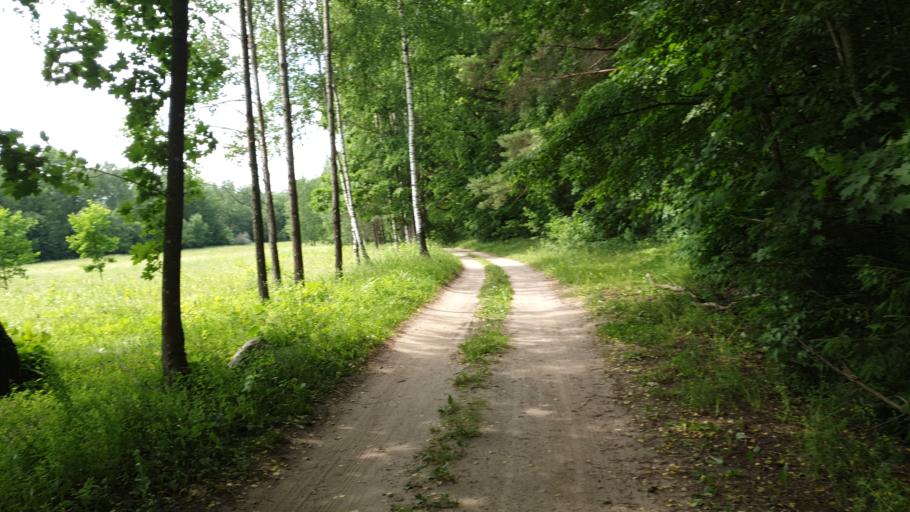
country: LT
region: Vilnius County
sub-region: Vilnius
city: Fabijoniskes
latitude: 54.7874
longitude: 25.3197
